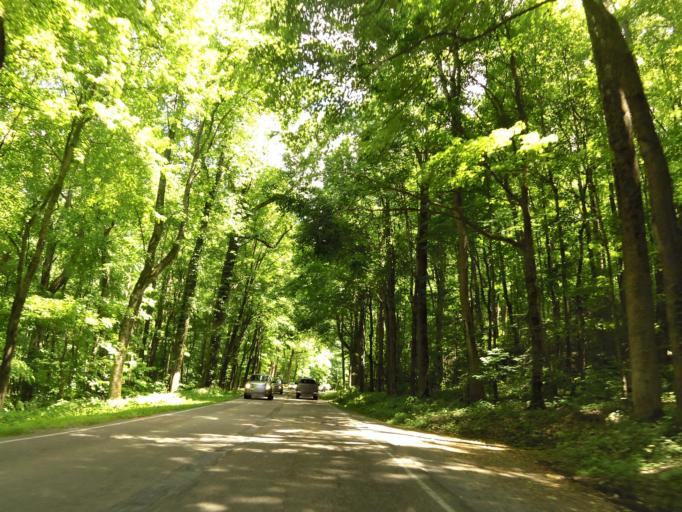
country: US
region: Tennessee
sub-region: Sevier County
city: Gatlinburg
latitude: 35.6472
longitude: -83.5116
